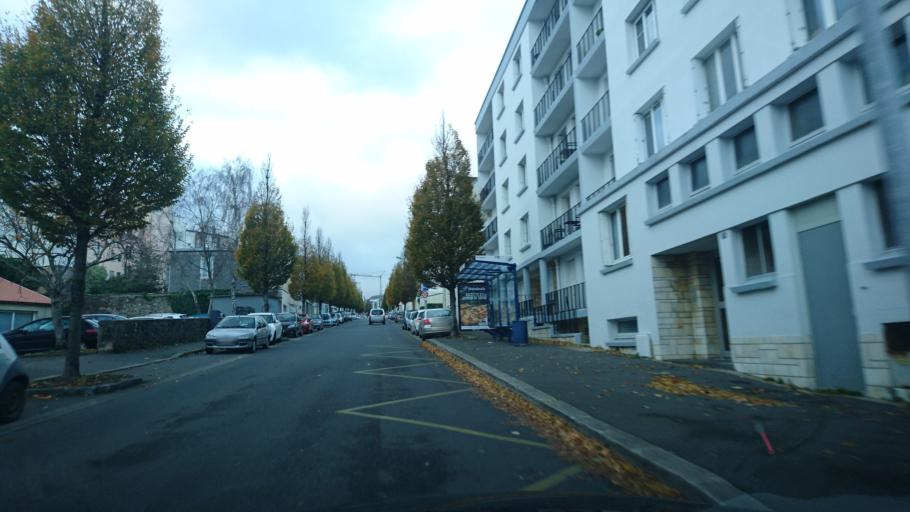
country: FR
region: Brittany
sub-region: Departement du Finistere
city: Brest
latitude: 48.3920
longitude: -4.4741
